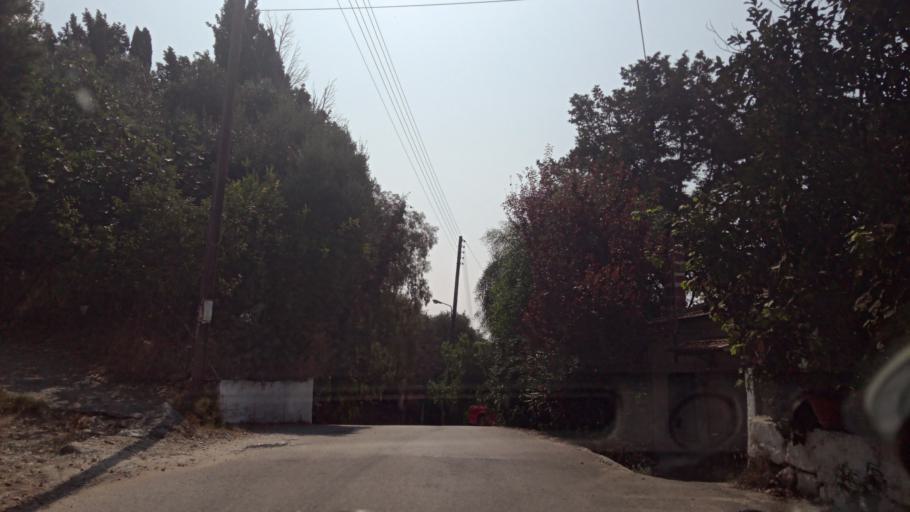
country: GR
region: Ionian Islands
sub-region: Nomos Kerkyras
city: Perivoli
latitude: 39.4097
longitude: 20.0234
